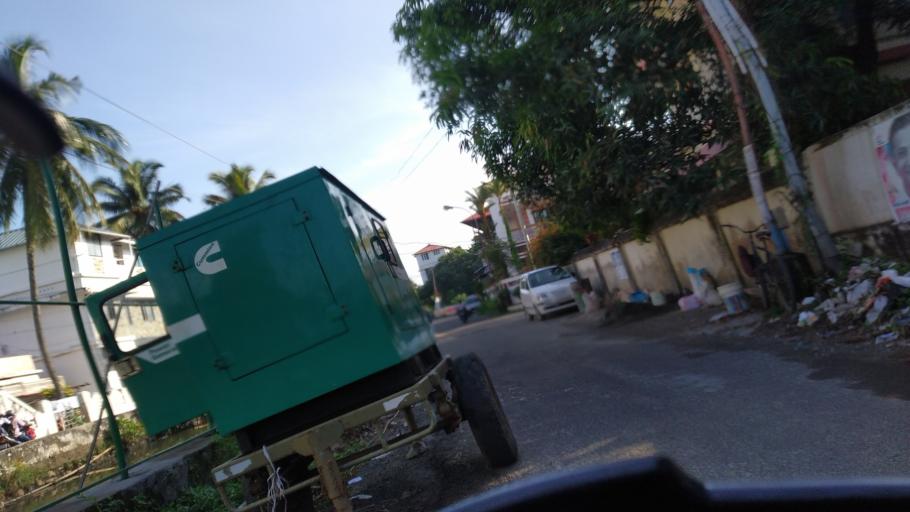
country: IN
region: Kerala
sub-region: Ernakulam
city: Cochin
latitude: 9.9869
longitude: 76.2913
